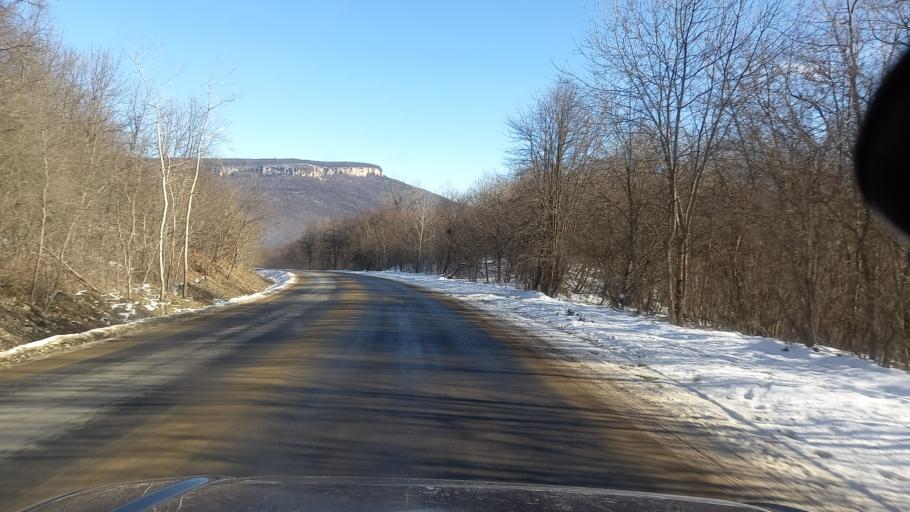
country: RU
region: Adygeya
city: Kamennomostskiy
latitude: 44.2395
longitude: 40.1754
